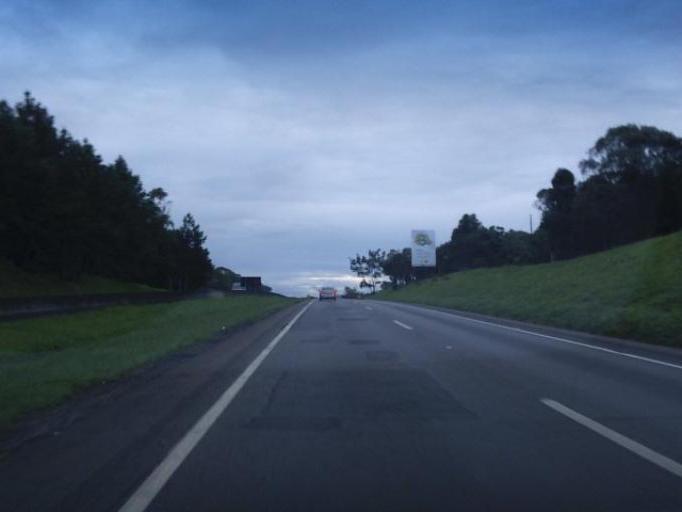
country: BR
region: Parana
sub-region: Sao Jose Dos Pinhais
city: Sao Jose dos Pinhais
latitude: -25.7984
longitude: -49.1317
